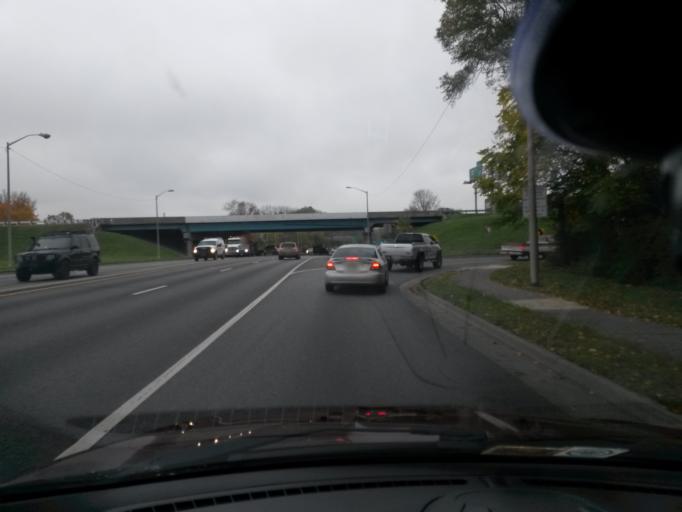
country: US
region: Virginia
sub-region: City of Roanoke
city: Roanoke
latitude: 37.2823
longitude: -79.9371
